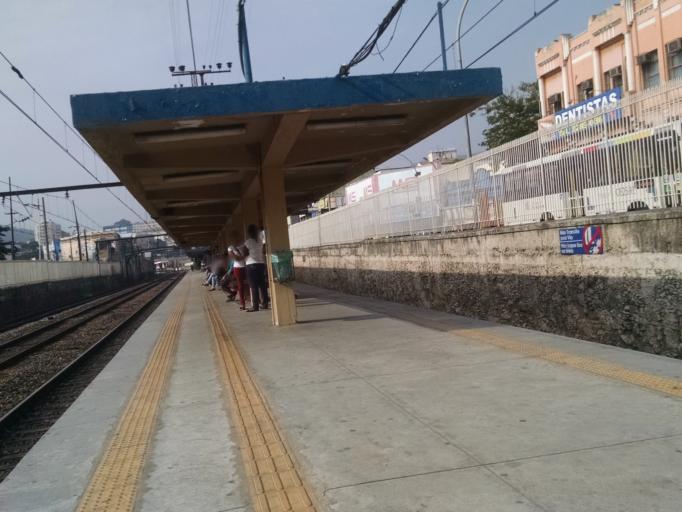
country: BR
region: Rio de Janeiro
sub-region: Rio De Janeiro
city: Rio de Janeiro
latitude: -22.9016
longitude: -43.2782
